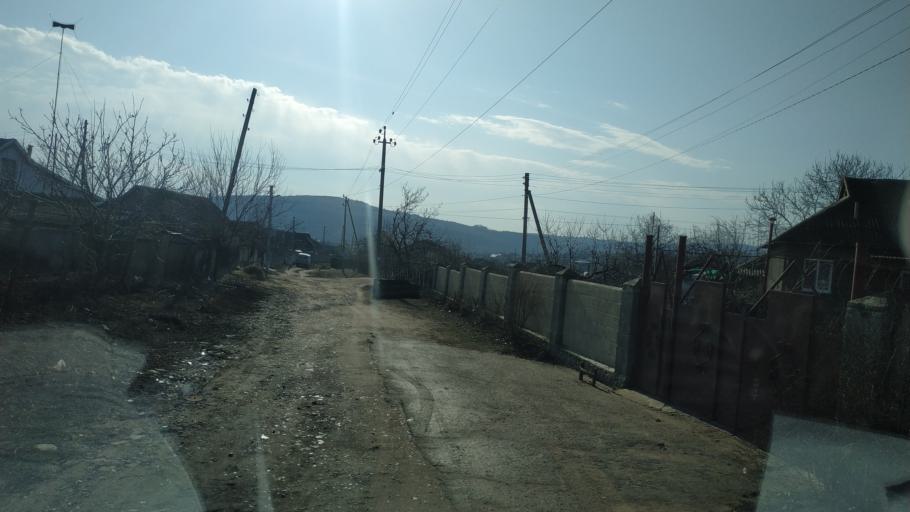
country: MD
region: Chisinau
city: Singera
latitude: 46.6867
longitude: 29.0416
